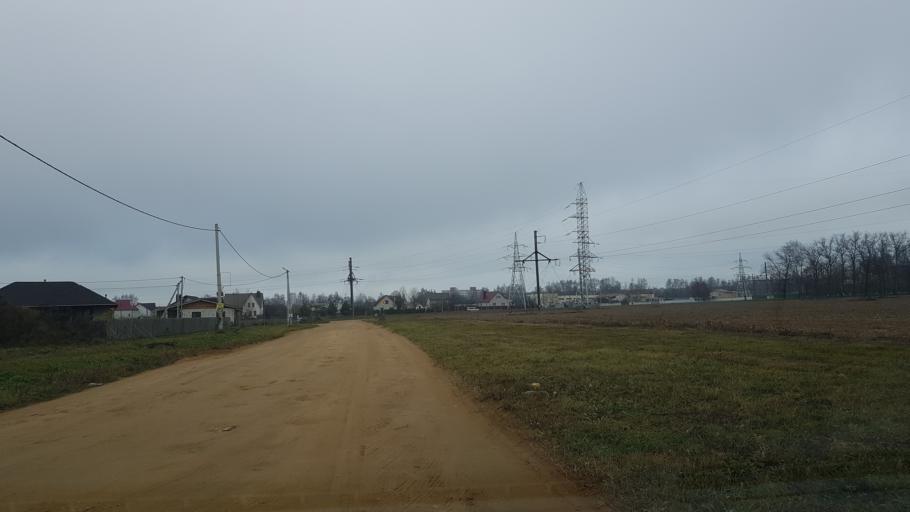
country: BY
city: Fanipol
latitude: 53.7331
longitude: 27.3262
